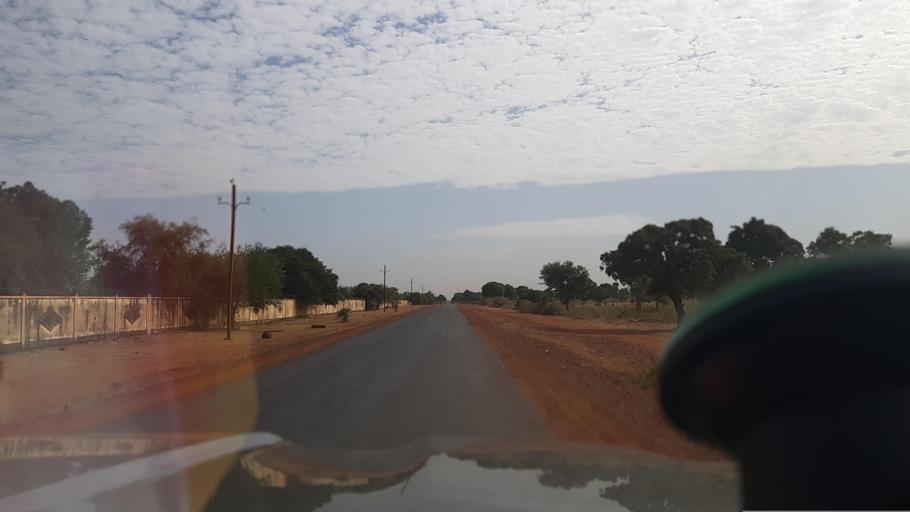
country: ML
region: Segou
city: Segou
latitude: 13.4979
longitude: -6.1600
